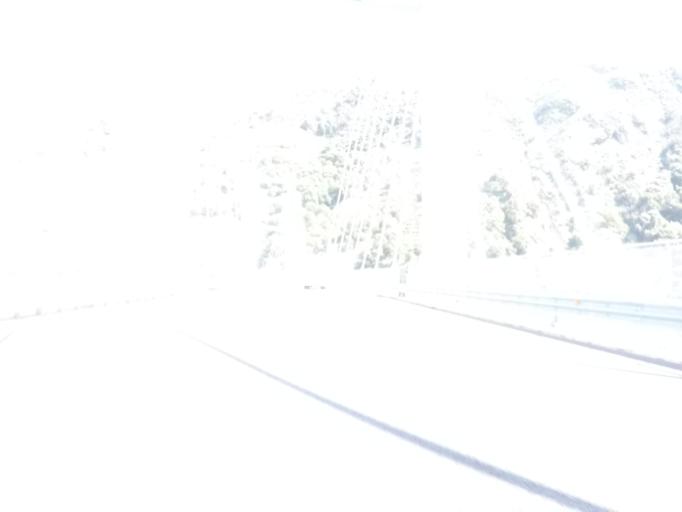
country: IT
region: Calabria
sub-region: Provincia di Reggio Calabria
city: Scilla
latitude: 38.2539
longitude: 15.7667
